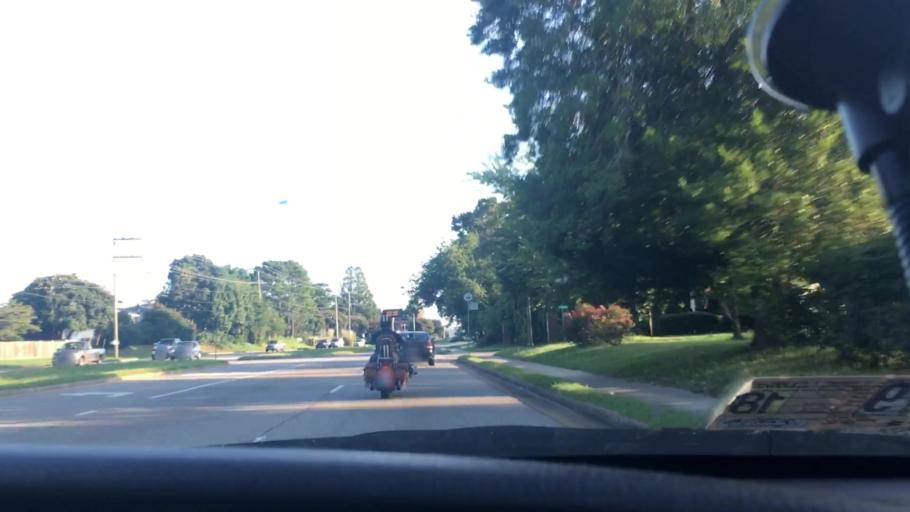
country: US
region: Virginia
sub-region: City of Chesapeake
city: Chesapeake
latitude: 36.8802
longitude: -76.1333
